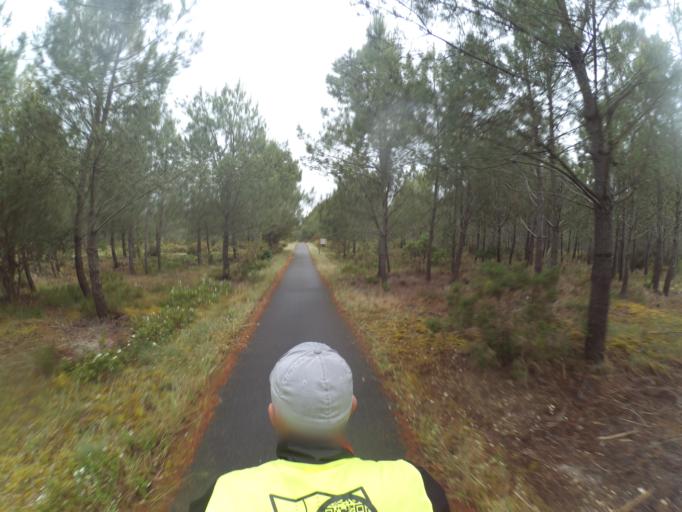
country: FR
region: Aquitaine
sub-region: Departement des Landes
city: Mimizan
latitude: 44.2235
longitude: -1.2582
